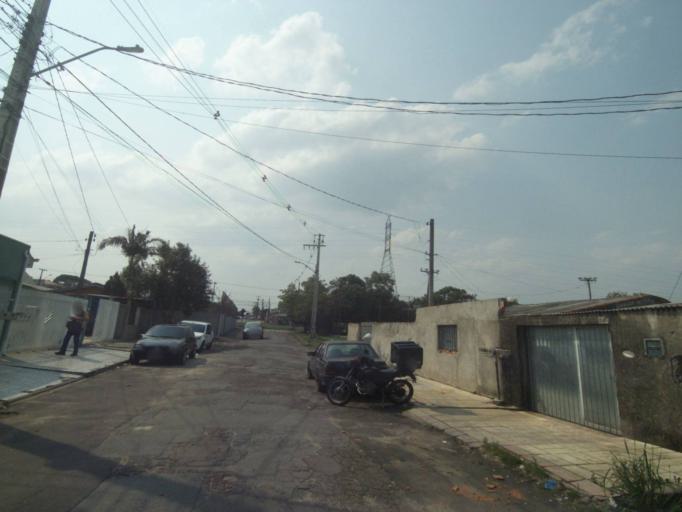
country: BR
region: Parana
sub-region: Sao Jose Dos Pinhais
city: Sao Jose dos Pinhais
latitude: -25.5271
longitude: -49.2347
